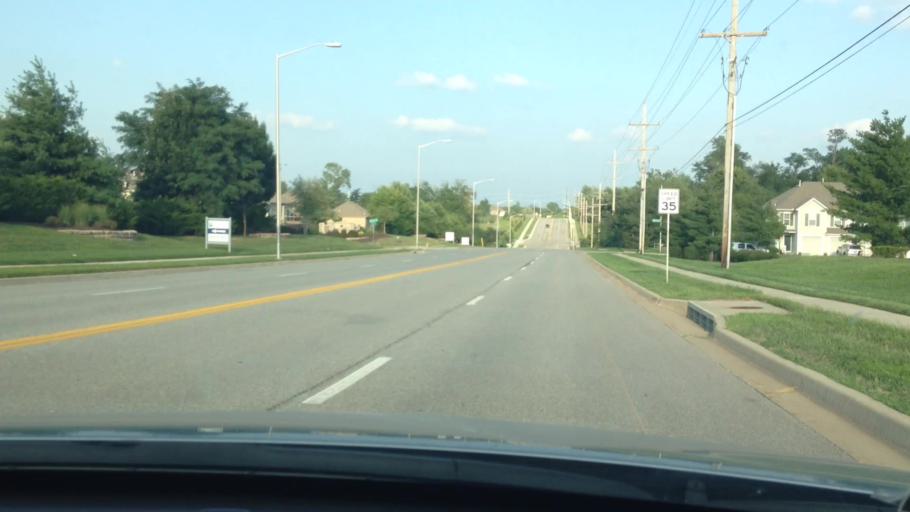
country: US
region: Missouri
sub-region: Platte County
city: Weatherby Lake
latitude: 39.2612
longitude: -94.6465
